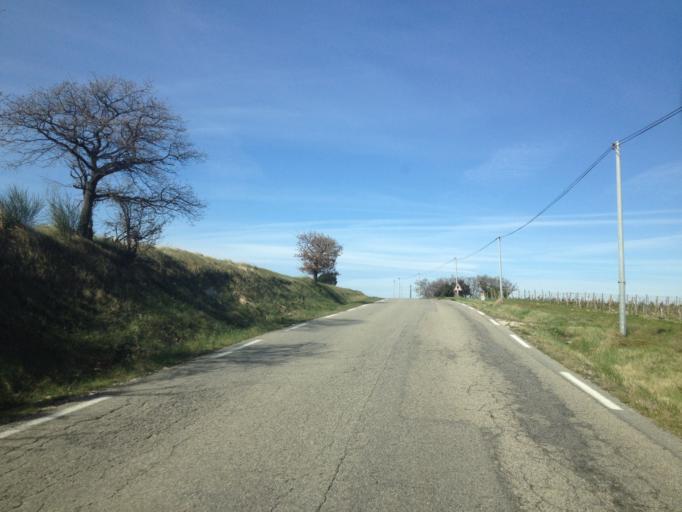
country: FR
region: Provence-Alpes-Cote d'Azur
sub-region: Departement du Vaucluse
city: Bedarrides
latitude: 44.0487
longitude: 4.8751
